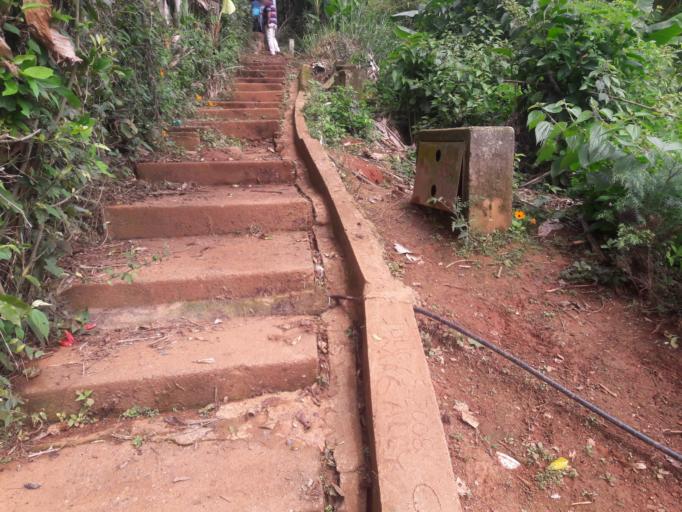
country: CO
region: Valle del Cauca
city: Cali
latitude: 3.4690
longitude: -76.6309
